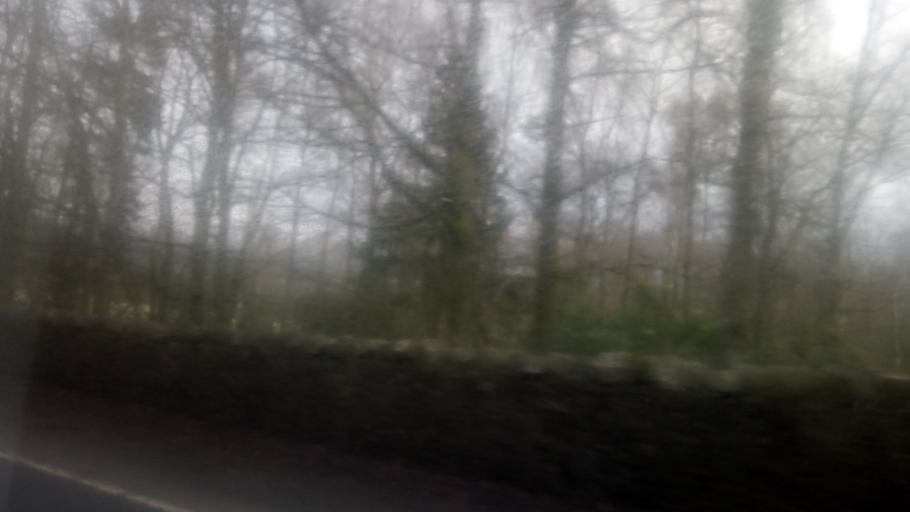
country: GB
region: Scotland
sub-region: The Scottish Borders
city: Lauder
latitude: 55.7311
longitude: -2.7640
